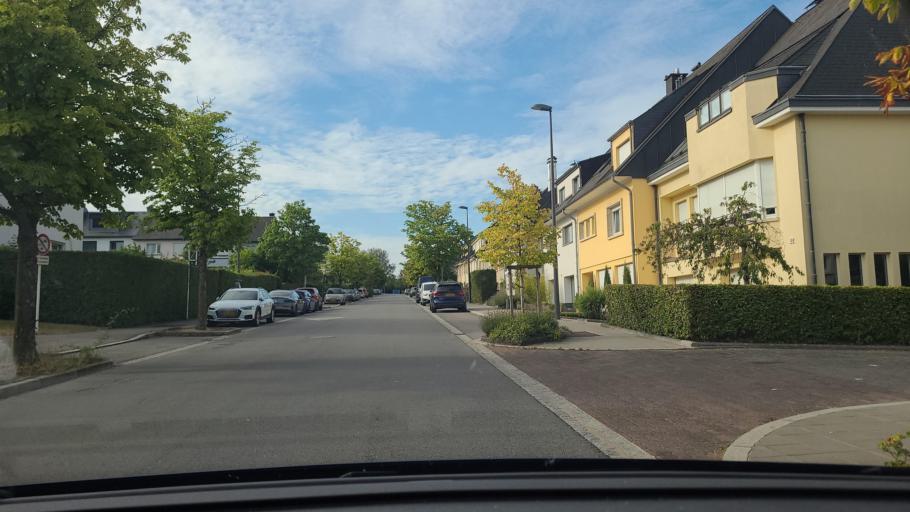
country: LU
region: Luxembourg
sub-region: Canton de Luxembourg
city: Luxembourg
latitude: 49.5955
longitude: 6.1502
